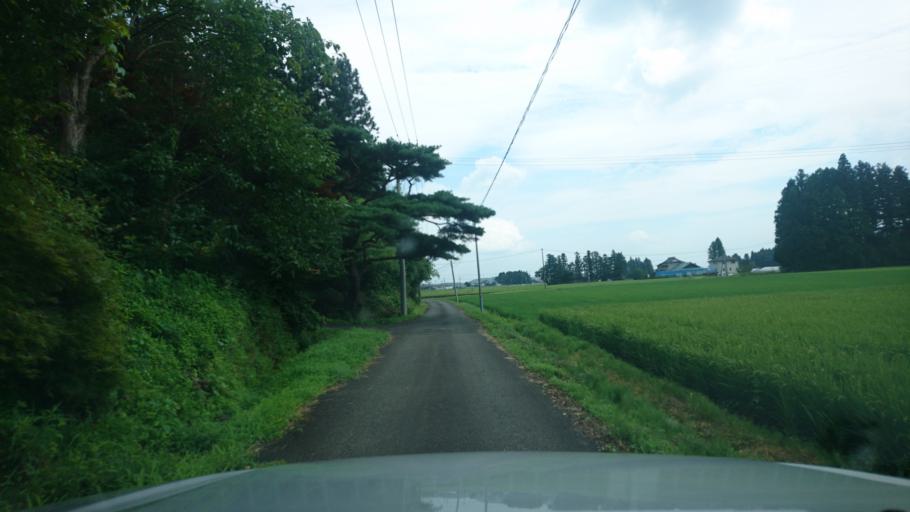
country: JP
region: Iwate
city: Ichinoseki
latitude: 38.8232
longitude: 140.9265
